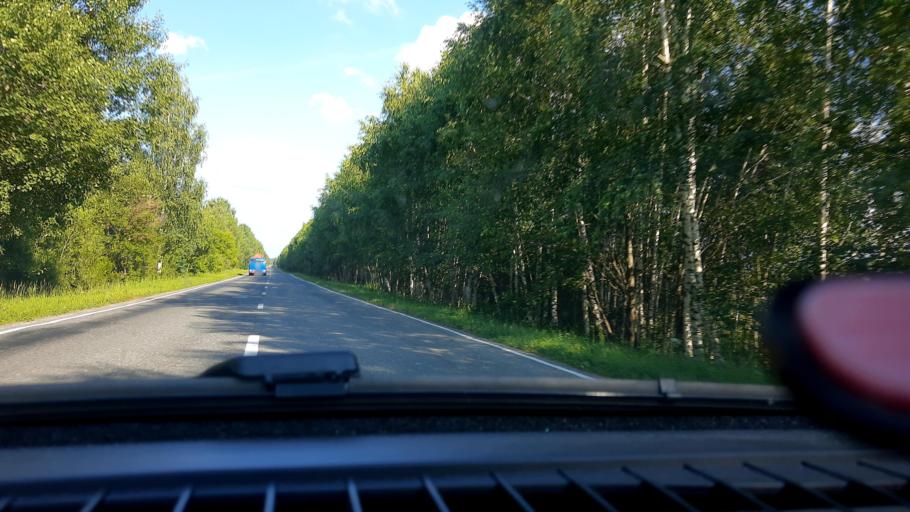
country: RU
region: Nizjnij Novgorod
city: Neklyudovo
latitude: 56.5157
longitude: 43.9299
